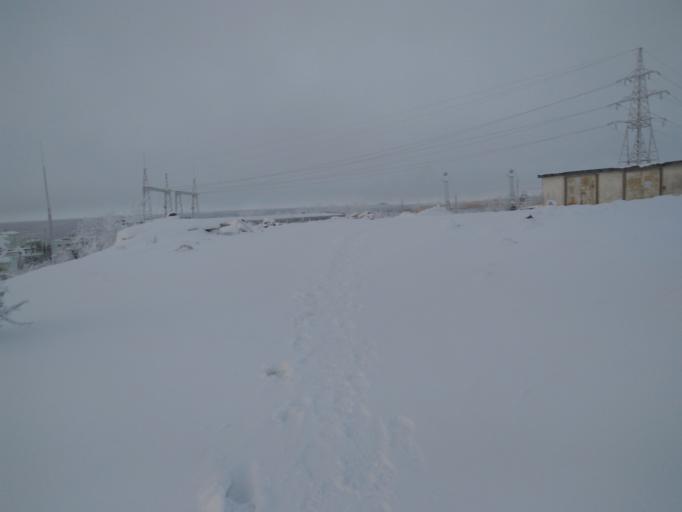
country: RU
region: Sakha
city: Aykhal
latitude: 65.9356
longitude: 111.5075
